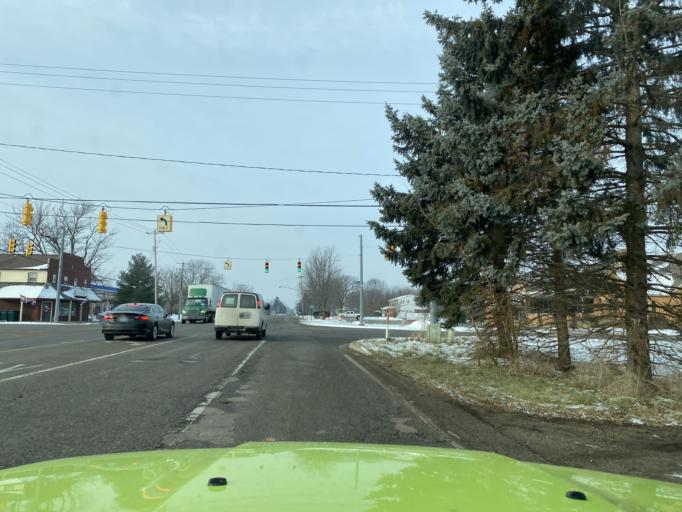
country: US
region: Michigan
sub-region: Ottawa County
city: Hudsonville
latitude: 42.8852
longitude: -85.9009
